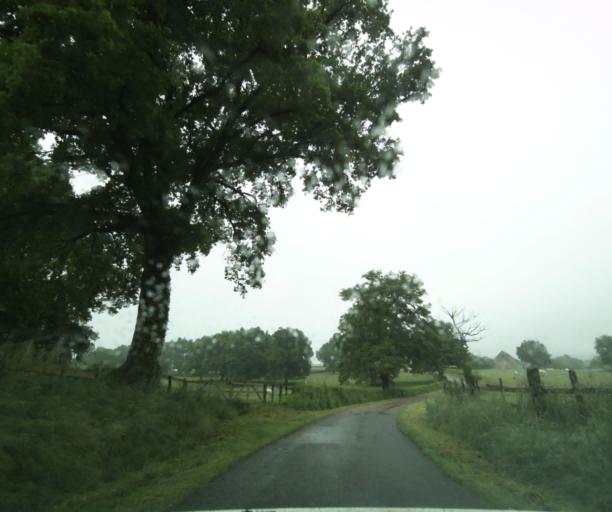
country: FR
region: Bourgogne
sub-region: Departement de Saone-et-Loire
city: Charolles
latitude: 46.4260
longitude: 4.3280
